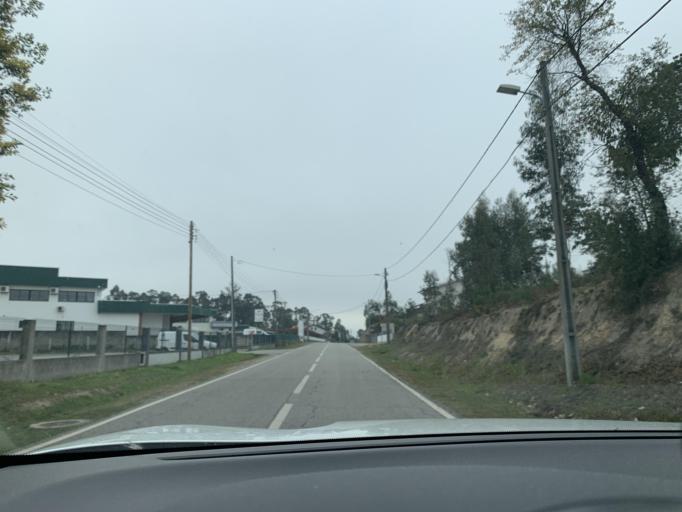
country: PT
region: Viseu
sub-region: Concelho de Tondela
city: Tondela
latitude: 40.5314
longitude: -8.0554
